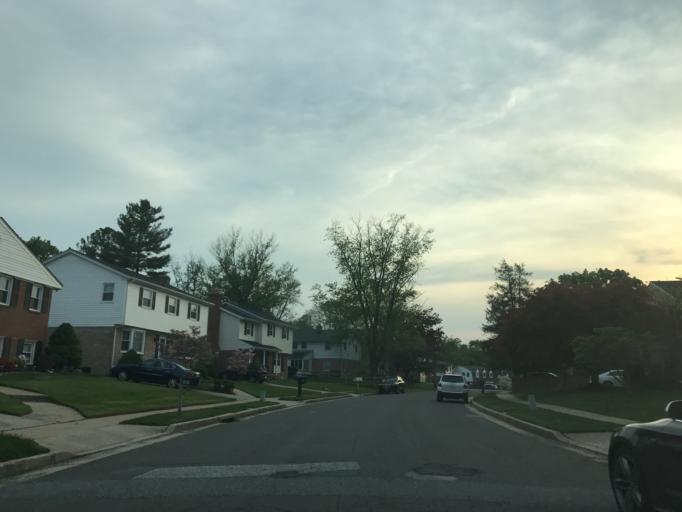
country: US
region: Maryland
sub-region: Baltimore County
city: Cockeysville
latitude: 39.4681
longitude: -76.6302
